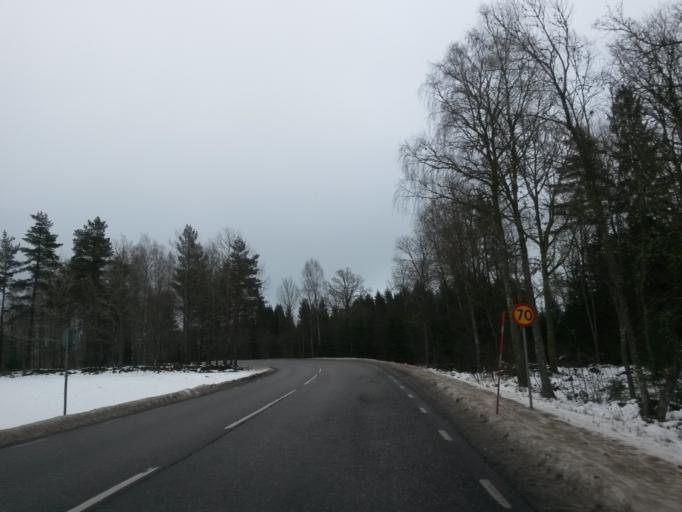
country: SE
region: Vaestra Goetaland
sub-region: Vargarda Kommun
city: Vargarda
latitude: 57.9880
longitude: 12.8893
